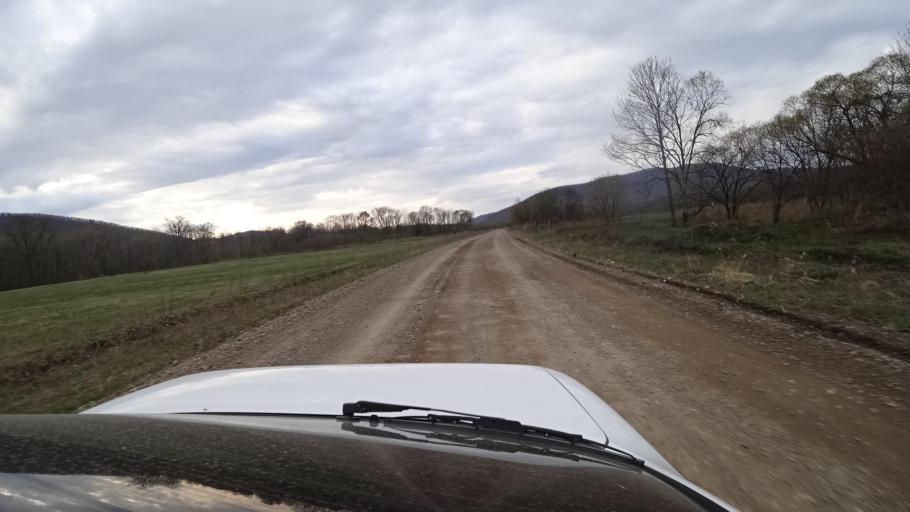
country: RU
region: Primorskiy
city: Novopokrovka
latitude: 45.1491
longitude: 134.3816
